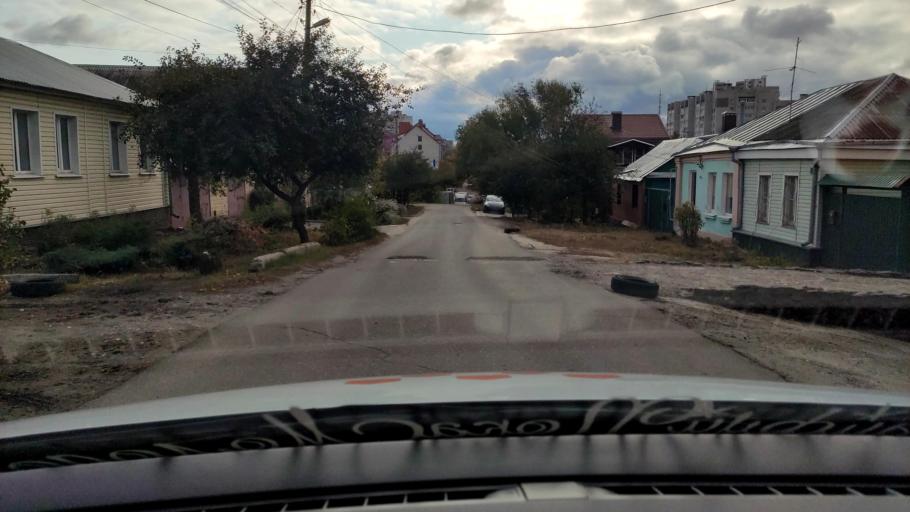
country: RU
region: Voronezj
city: Voronezh
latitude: 51.6918
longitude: 39.2015
